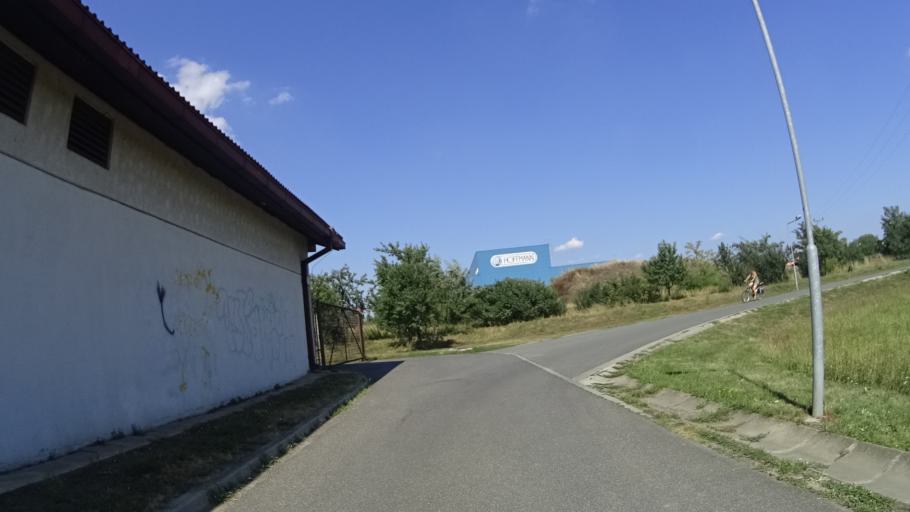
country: CZ
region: Zlin
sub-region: Okres Zlin
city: Ostrozska Nova Ves
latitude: 49.0019
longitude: 17.4270
